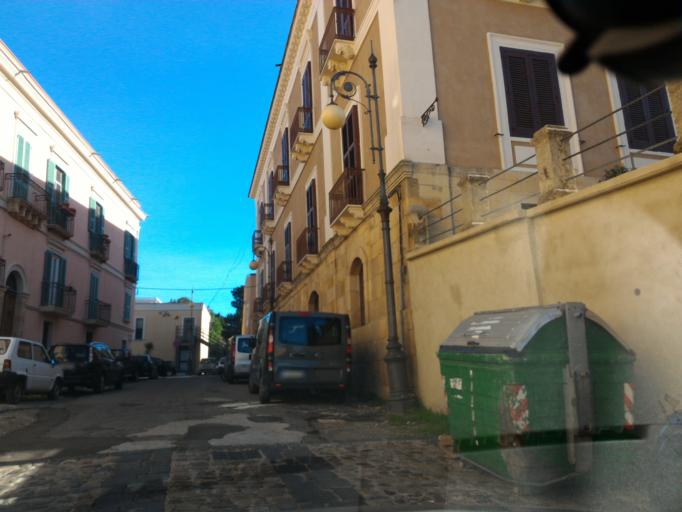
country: IT
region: Calabria
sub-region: Provincia di Crotone
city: Crotone
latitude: 39.0799
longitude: 17.1305
